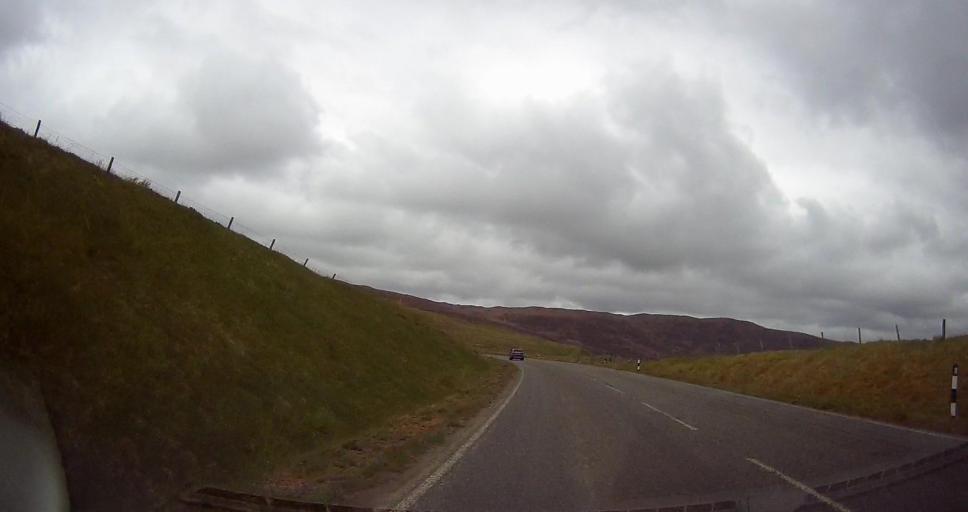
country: GB
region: Scotland
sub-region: Shetland Islands
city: Lerwick
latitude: 60.3705
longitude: -1.3272
